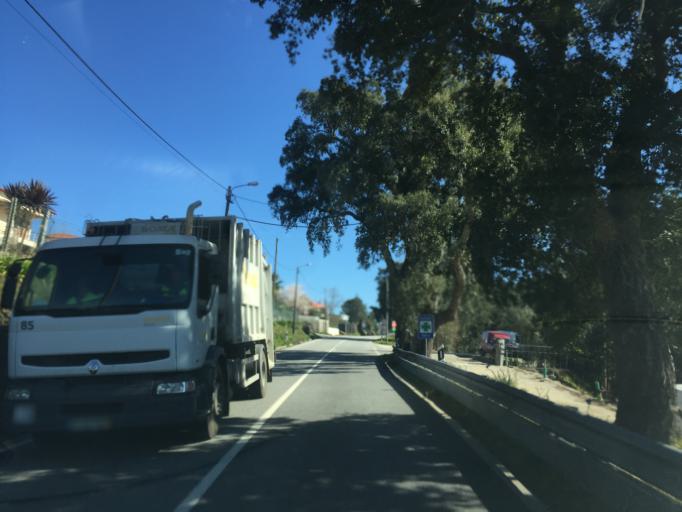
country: PT
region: Aveiro
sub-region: Vale de Cambra
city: Macieira de Cambra
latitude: 40.8890
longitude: -8.3478
